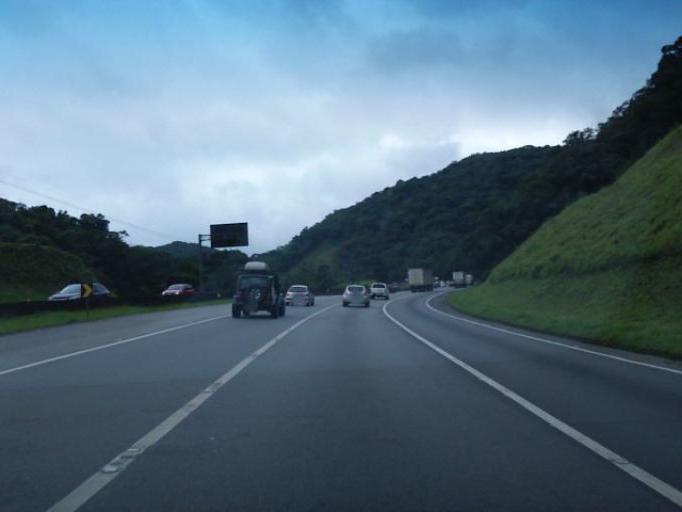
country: BR
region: Parana
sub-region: Guaratuba
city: Guaratuba
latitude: -25.8673
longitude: -48.9337
